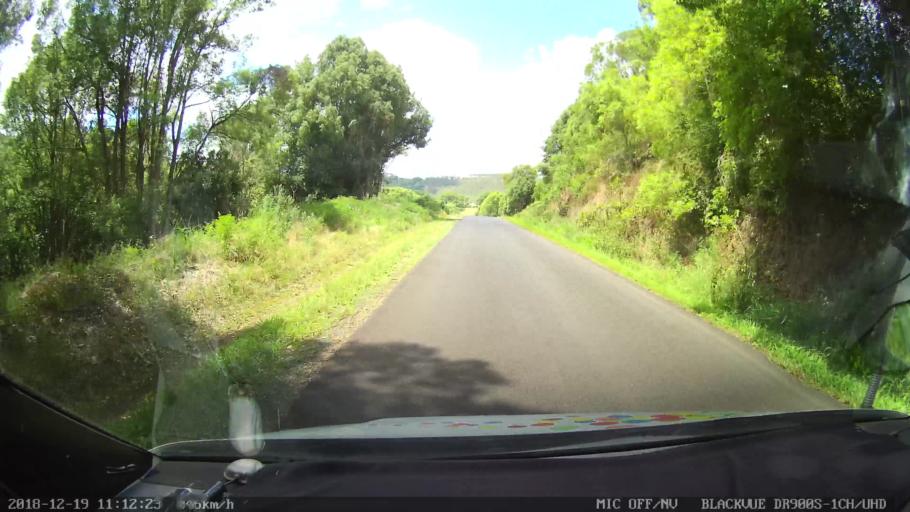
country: AU
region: New South Wales
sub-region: Lismore Municipality
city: Nimbin
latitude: -28.6486
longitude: 153.2605
